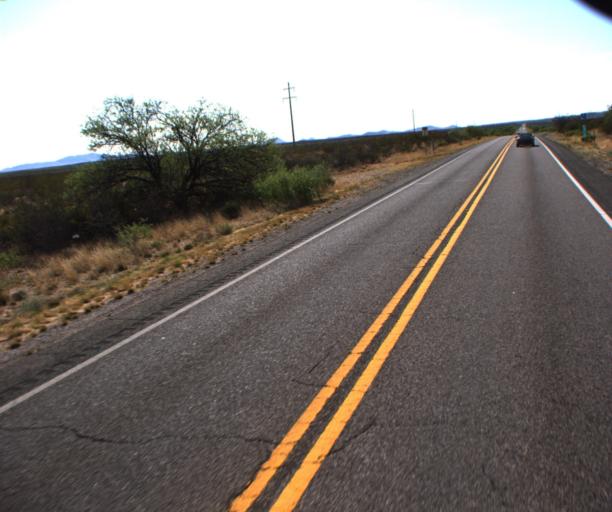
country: US
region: Arizona
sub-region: Cochise County
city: Tombstone
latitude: 31.7682
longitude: -110.1215
